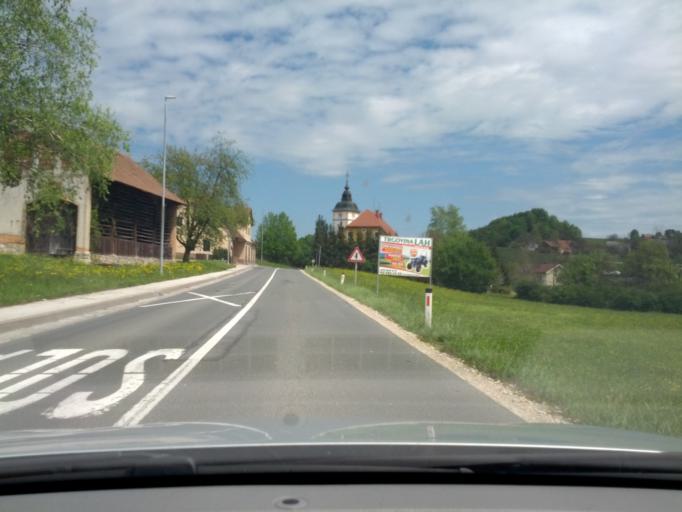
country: SI
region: Smarje pri Jelsah
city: Smarje pri Jelsah
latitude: 46.2256
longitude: 15.4649
